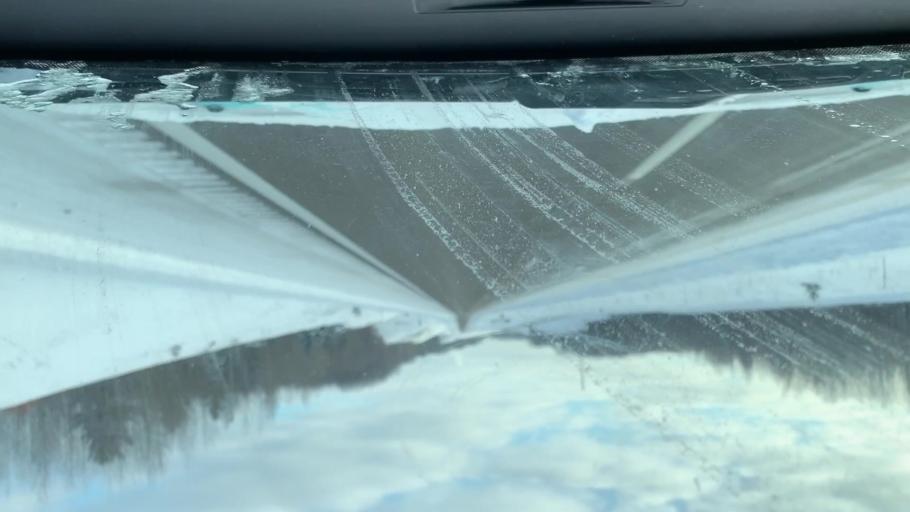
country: US
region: Michigan
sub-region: Wexford County
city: Manton
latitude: 44.3447
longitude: -85.4053
